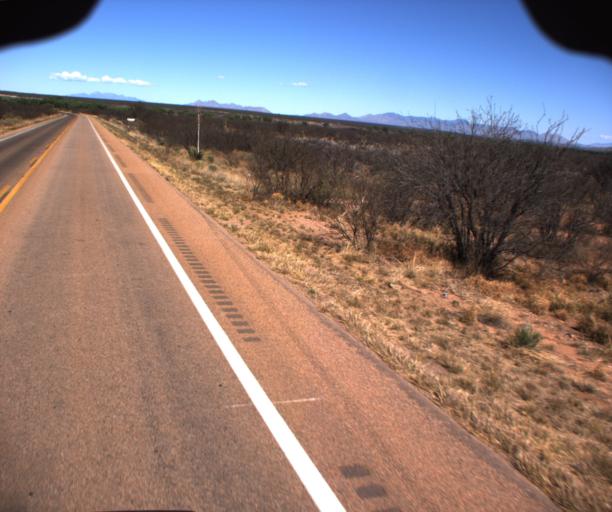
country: US
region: Arizona
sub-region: Cochise County
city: Sierra Vista Southeast
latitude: 31.5533
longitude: -110.1262
